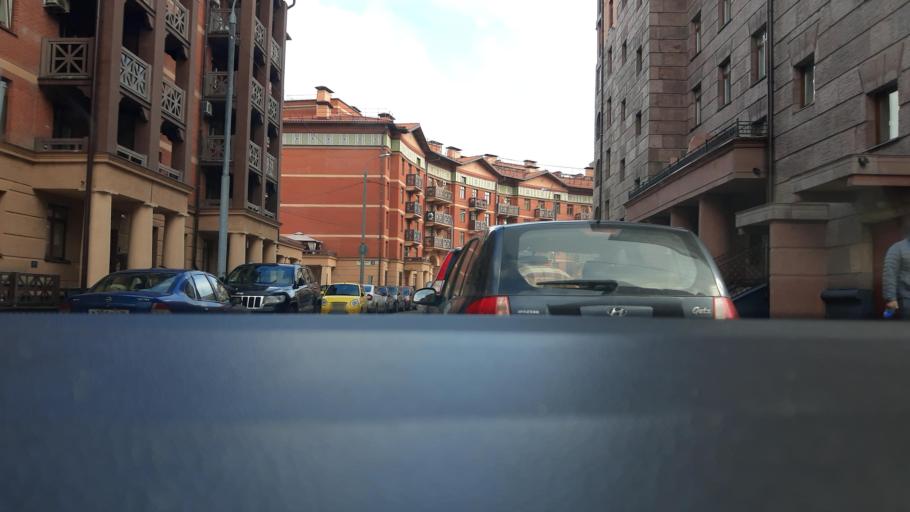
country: RU
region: Moskovskaya
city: Sheremet'yevskiy
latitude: 55.9594
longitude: 37.4408
